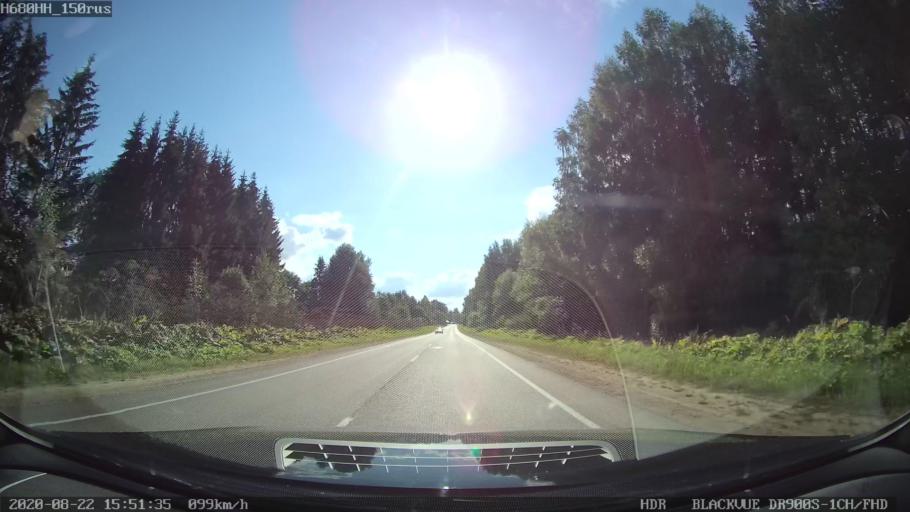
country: RU
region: Tverskaya
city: Bezhetsk
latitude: 57.6636
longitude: 36.4222
